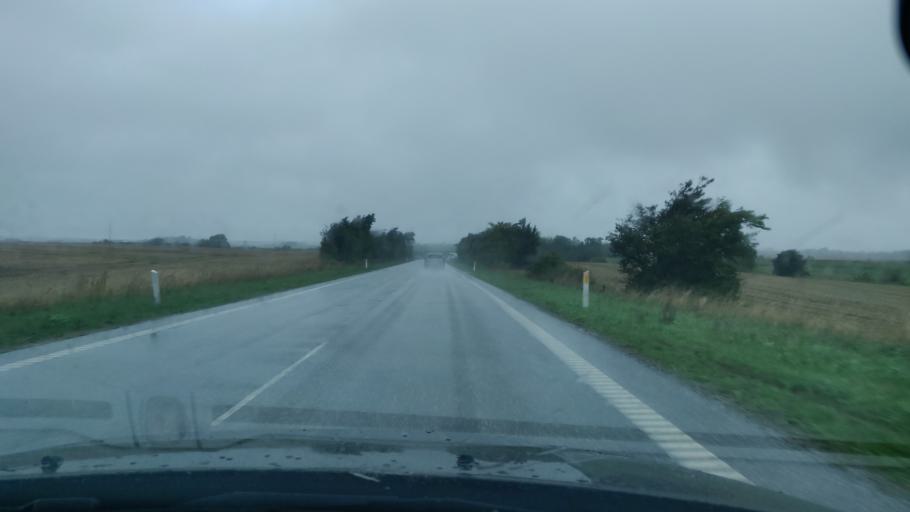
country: DK
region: North Denmark
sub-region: Thisted Kommune
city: Hurup
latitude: 56.8504
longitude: 8.5398
